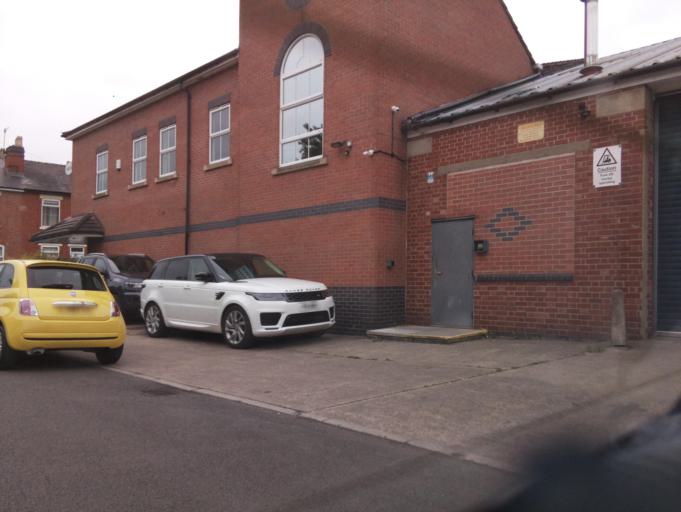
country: GB
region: England
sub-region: Derby
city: Derby
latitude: 52.9130
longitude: -1.4914
